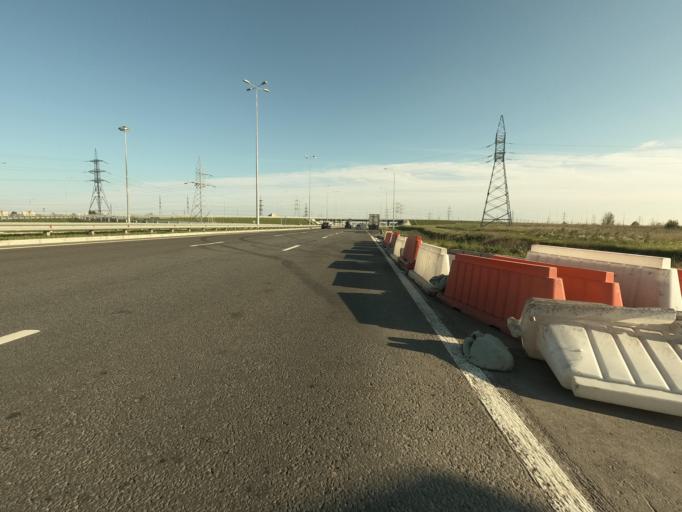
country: RU
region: St.-Petersburg
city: Kolpino
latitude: 59.7454
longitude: 30.5366
